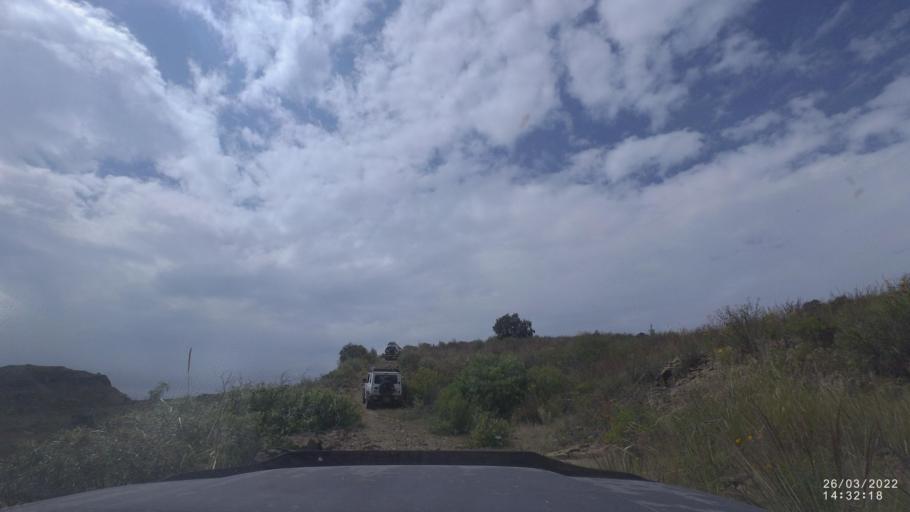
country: BO
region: Cochabamba
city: Cliza
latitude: -17.7427
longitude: -65.8680
